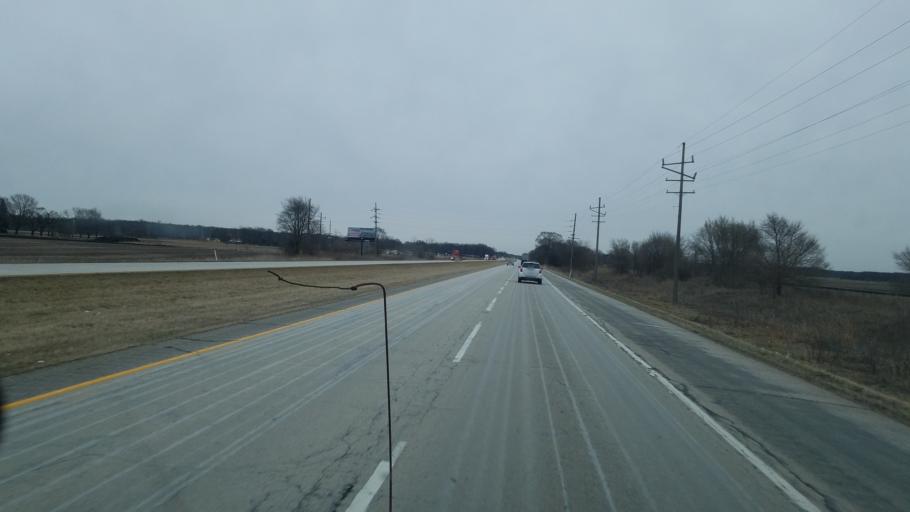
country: US
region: Indiana
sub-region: Starke County
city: Koontz Lake
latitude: 41.3749
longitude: -86.5299
